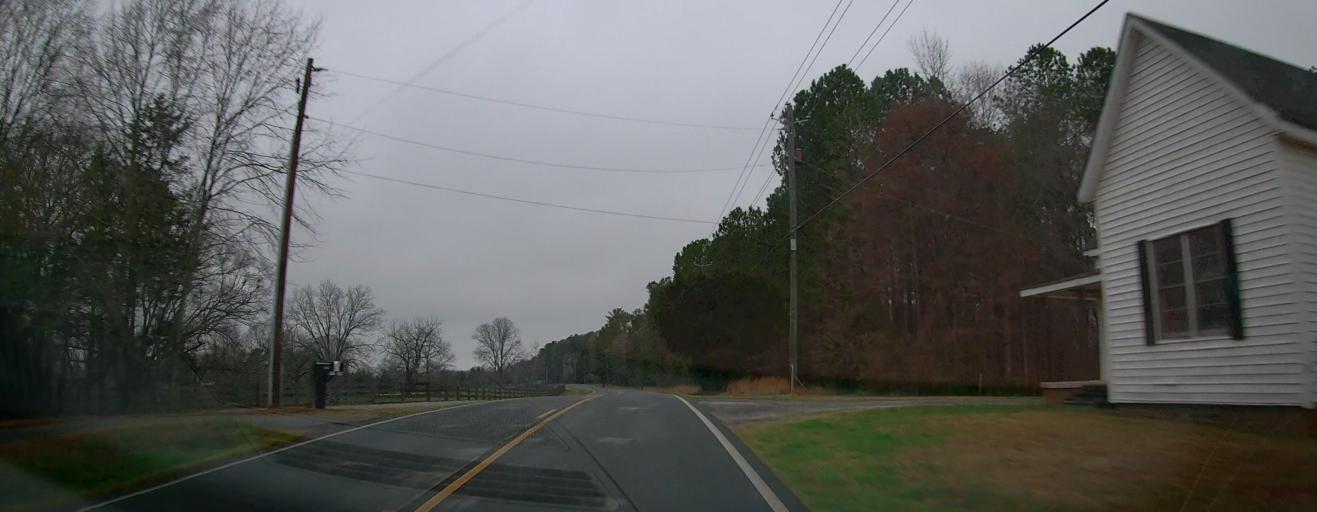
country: US
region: Georgia
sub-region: Pike County
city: Zebulon
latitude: 33.1398
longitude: -84.3459
